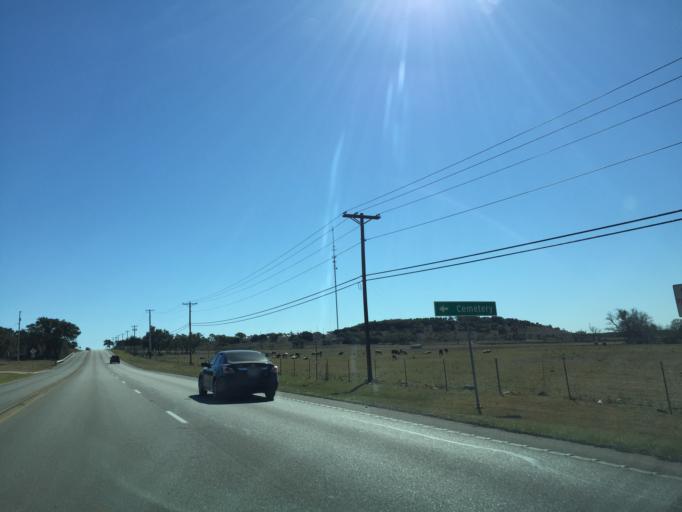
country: US
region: Texas
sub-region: Comal County
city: Canyon Lake
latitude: 29.7856
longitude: -98.3278
